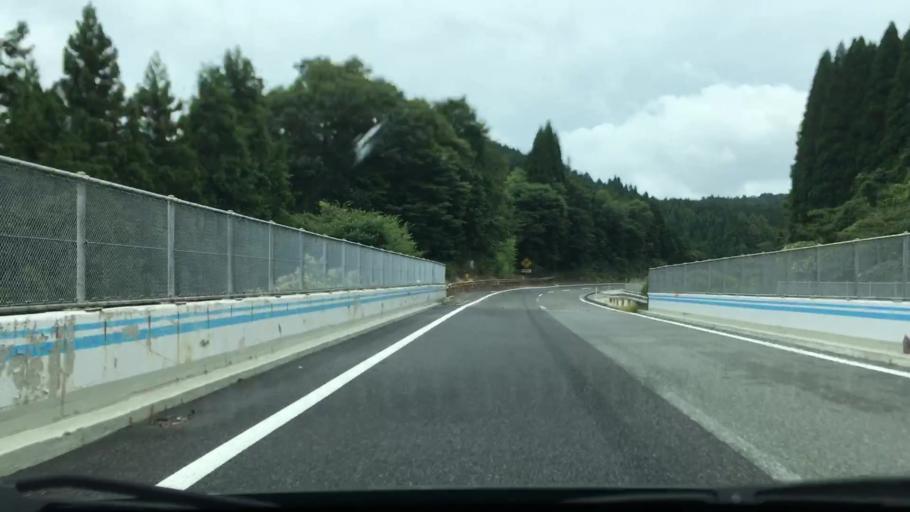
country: JP
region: Hiroshima
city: Shobara
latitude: 34.8806
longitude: 133.1915
